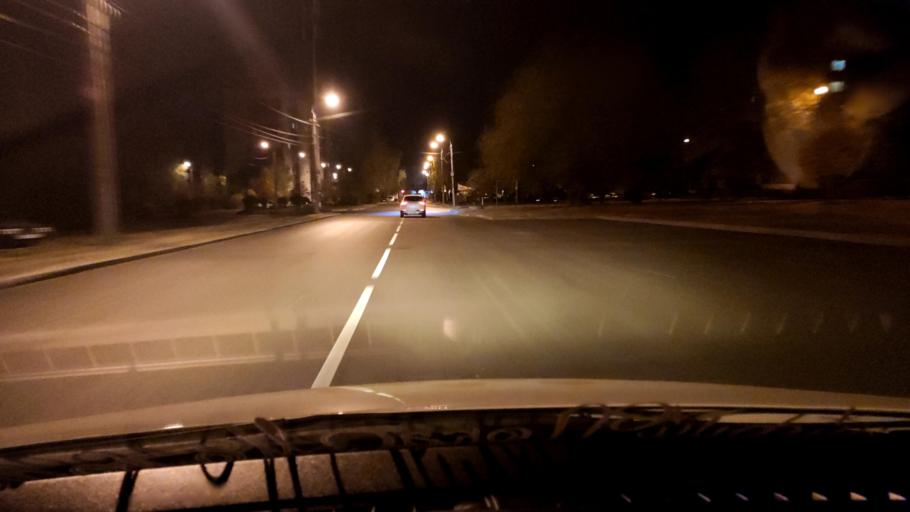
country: RU
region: Voronezj
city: Pridonskoy
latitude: 51.6816
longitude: 39.0895
